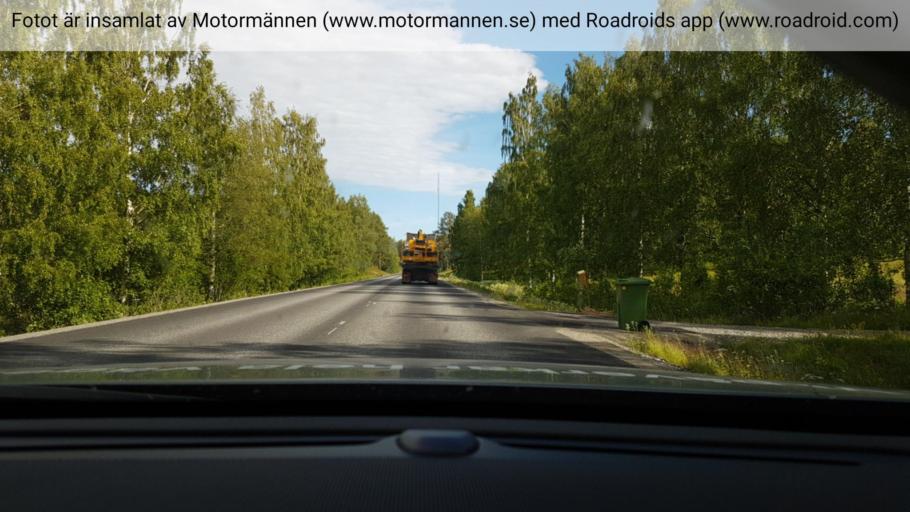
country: SE
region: Vaesterbotten
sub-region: Lycksele Kommun
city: Soderfors
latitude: 64.8347
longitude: 18.0012
